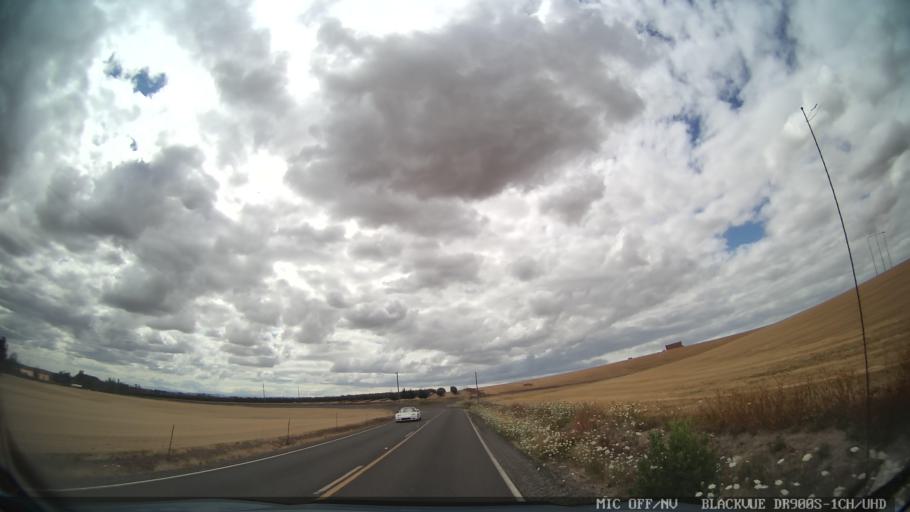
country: US
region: Oregon
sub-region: Marion County
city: Sublimity
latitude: 44.8478
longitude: -122.7515
